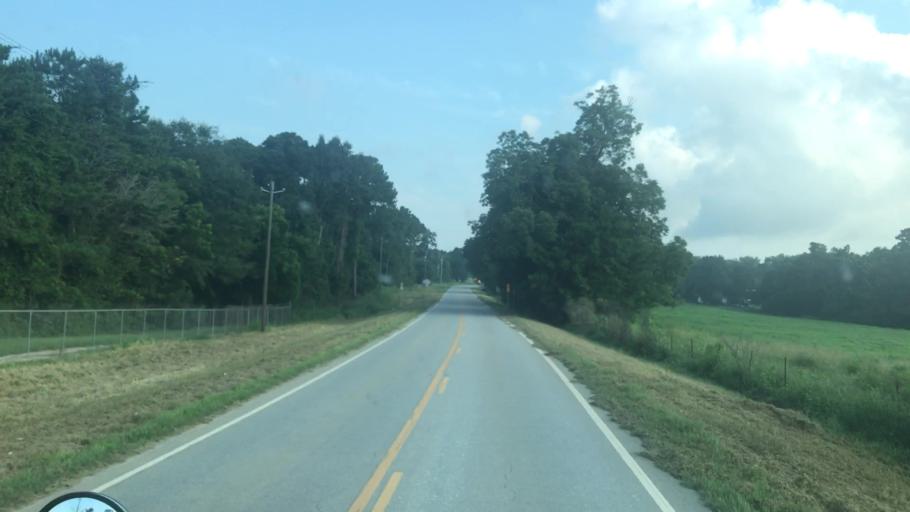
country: US
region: Florida
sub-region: Gadsden County
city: Havana
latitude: 30.7409
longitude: -84.4818
